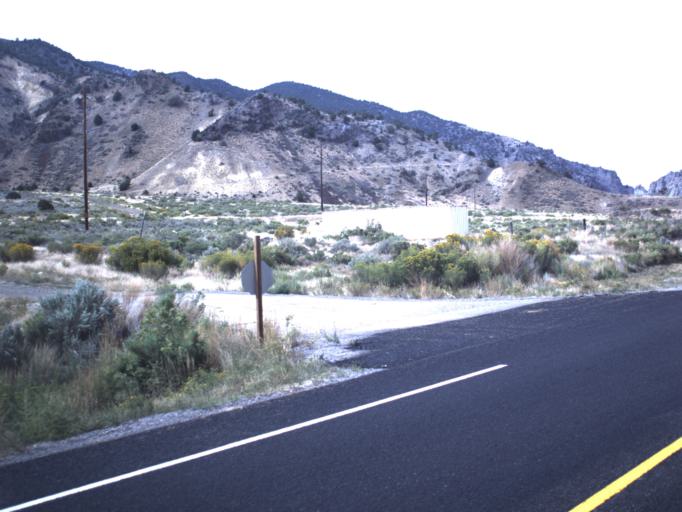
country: US
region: Utah
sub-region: Sevier County
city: Monroe
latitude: 38.5199
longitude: -112.2660
